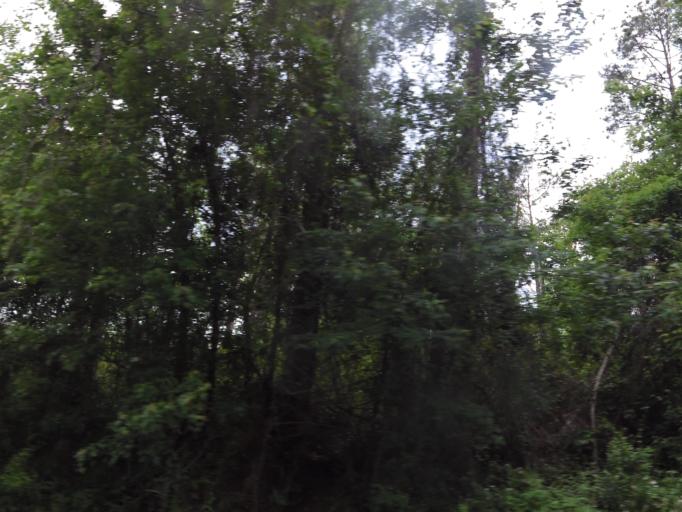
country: US
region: Georgia
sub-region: Charlton County
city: Folkston
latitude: 30.8178
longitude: -82.0708
